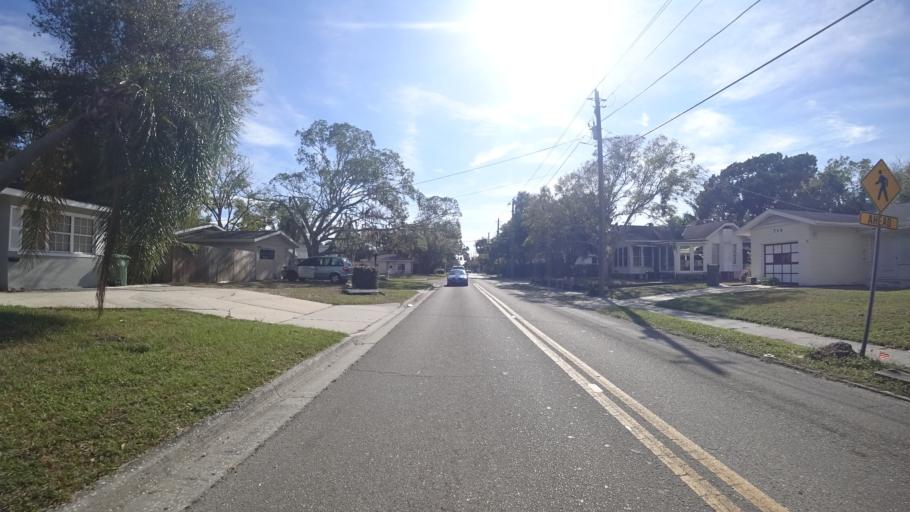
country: US
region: Florida
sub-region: Manatee County
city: Bradenton
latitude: 27.4932
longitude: -82.5875
